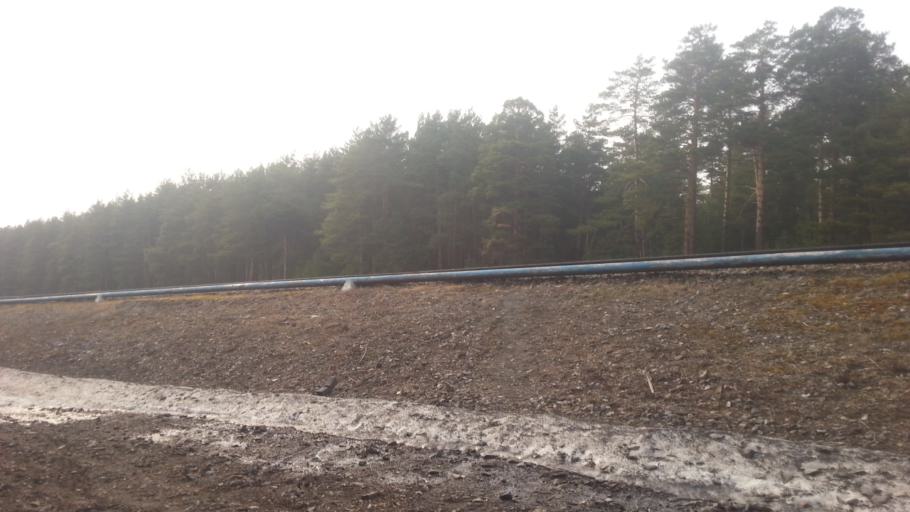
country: RU
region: Altai Krai
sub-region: Gorod Barnaulskiy
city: Barnaul
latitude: 53.3248
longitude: 83.7152
